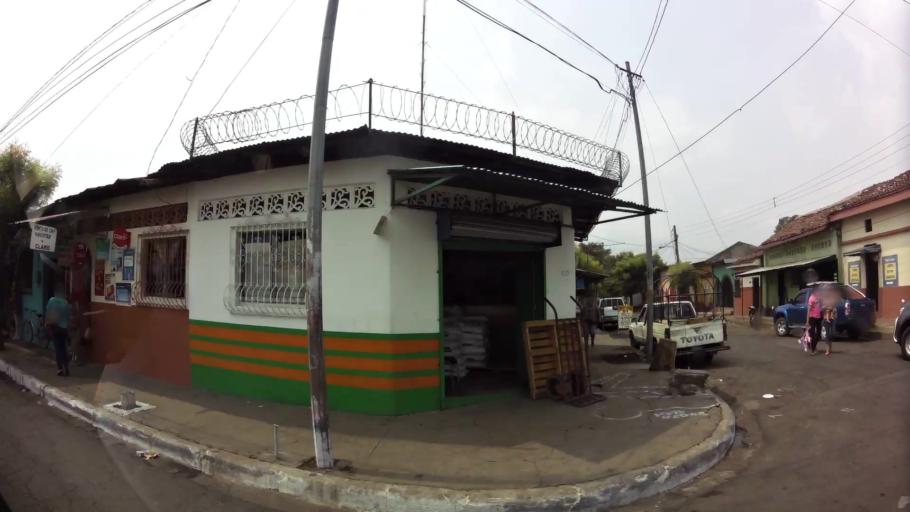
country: NI
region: Chinandega
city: Chinandega
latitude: 12.6336
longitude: -87.1342
